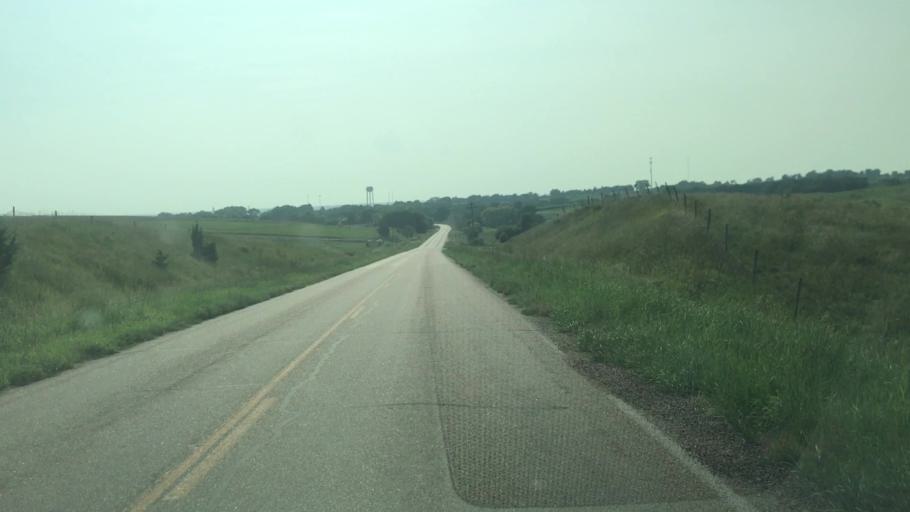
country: US
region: Nebraska
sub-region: Sherman County
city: Loup City
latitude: 41.2793
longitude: -98.9462
